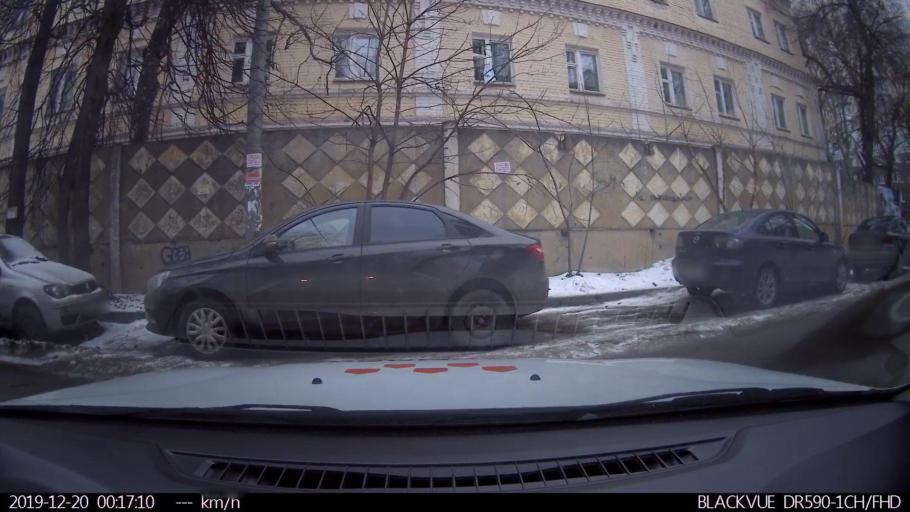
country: RU
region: Jaroslavl
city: Petrovsk
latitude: 56.9297
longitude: 39.4147
